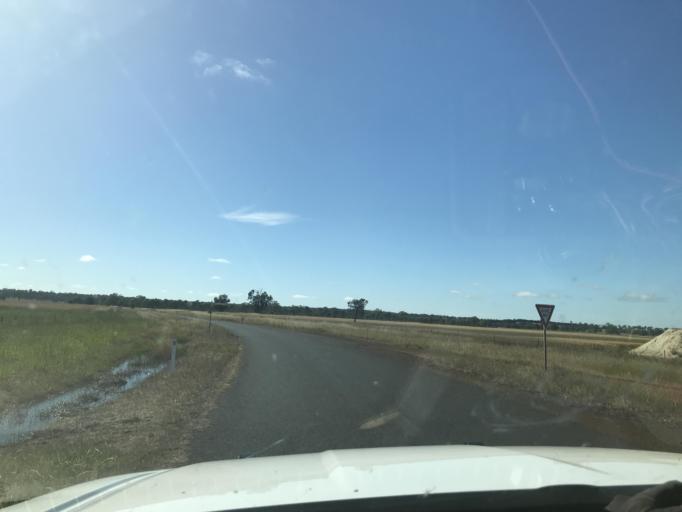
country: AU
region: Victoria
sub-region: Horsham
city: Horsham
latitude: -37.0831
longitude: 141.7476
